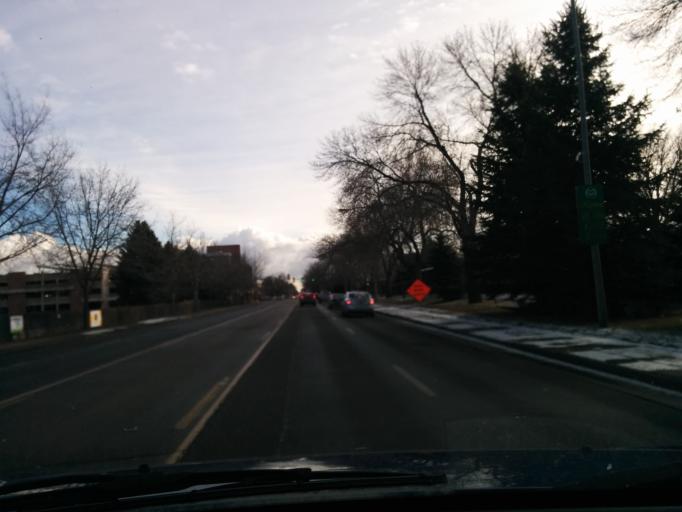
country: US
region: Colorado
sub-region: Larimer County
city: Fort Collins
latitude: 40.5671
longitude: -105.0860
